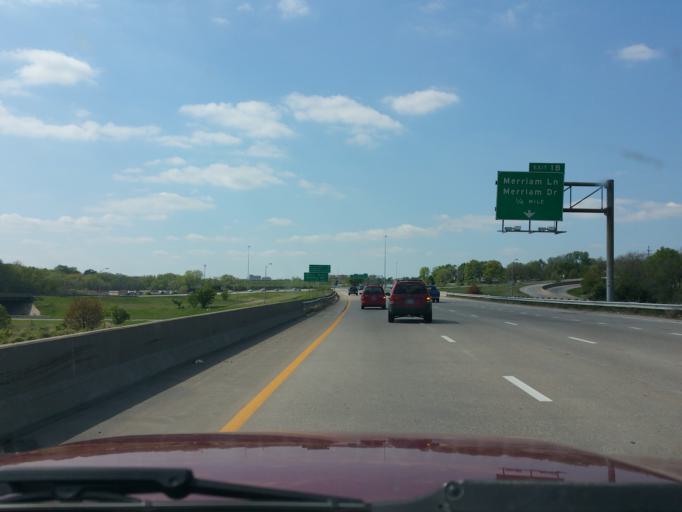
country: US
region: Kansas
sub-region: Johnson County
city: Mission
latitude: 39.0415
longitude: -94.6729
